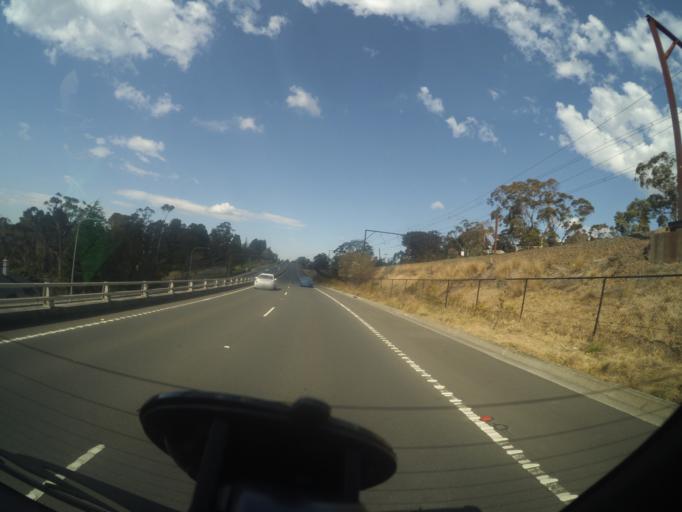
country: AU
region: New South Wales
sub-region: Blue Mountains Municipality
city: Leura
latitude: -33.7085
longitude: 150.3237
